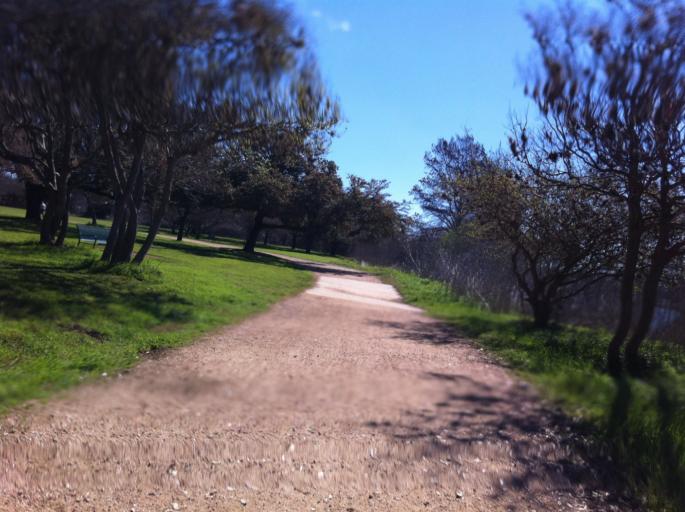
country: US
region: Texas
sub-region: Travis County
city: Austin
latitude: 30.2479
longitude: -97.7268
